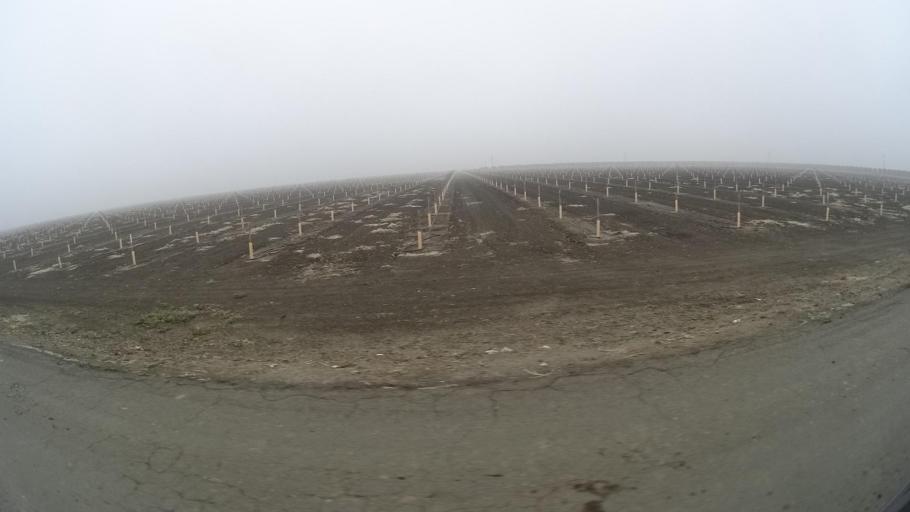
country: US
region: California
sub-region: Kern County
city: Buttonwillow
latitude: 35.4564
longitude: -119.5346
